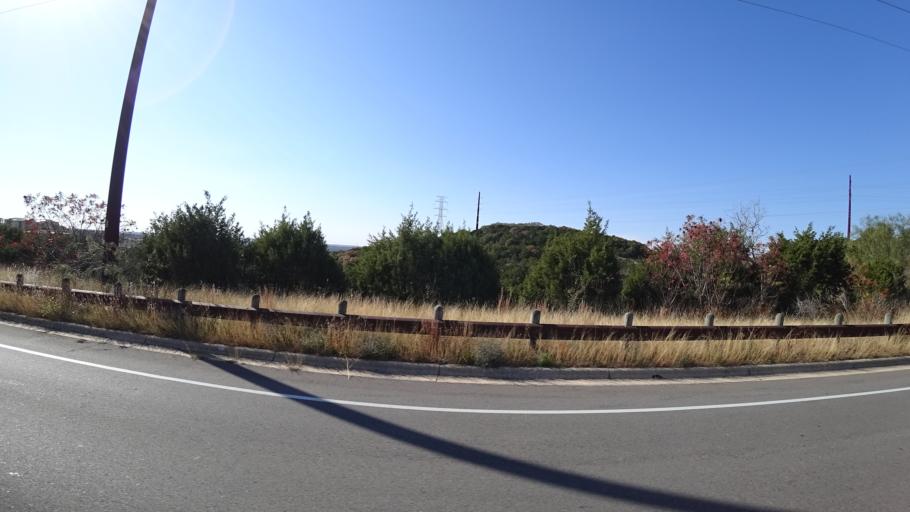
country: US
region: Texas
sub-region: Travis County
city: Hudson Bend
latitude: 30.3878
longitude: -97.8708
